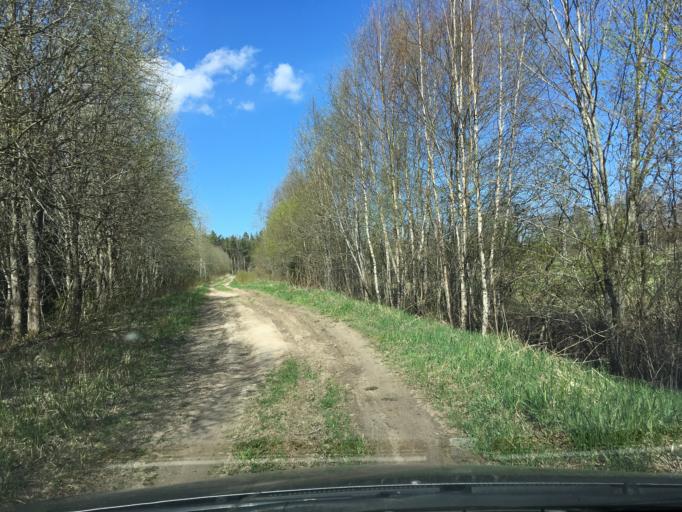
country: EE
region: Harju
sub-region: Raasiku vald
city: Arukula
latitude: 59.2073
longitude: 25.1203
